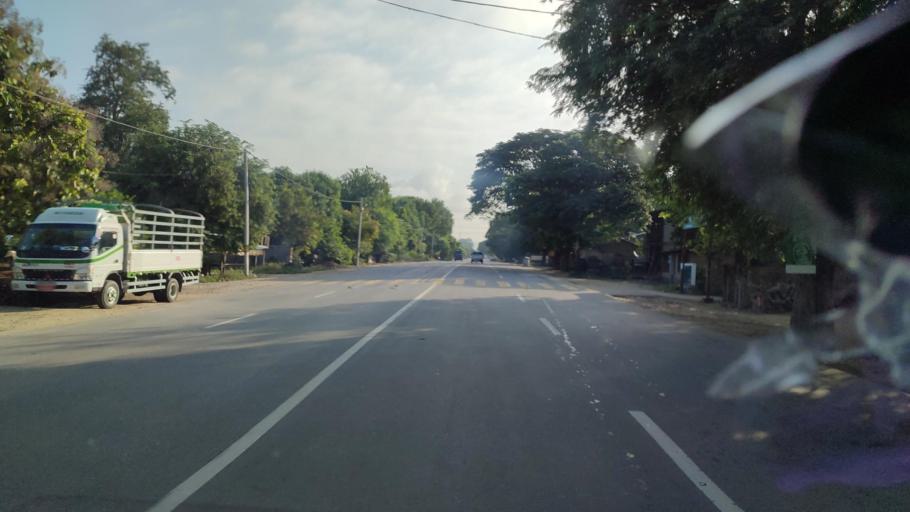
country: MM
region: Mandalay
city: Yamethin
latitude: 20.7523
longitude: 96.2389
